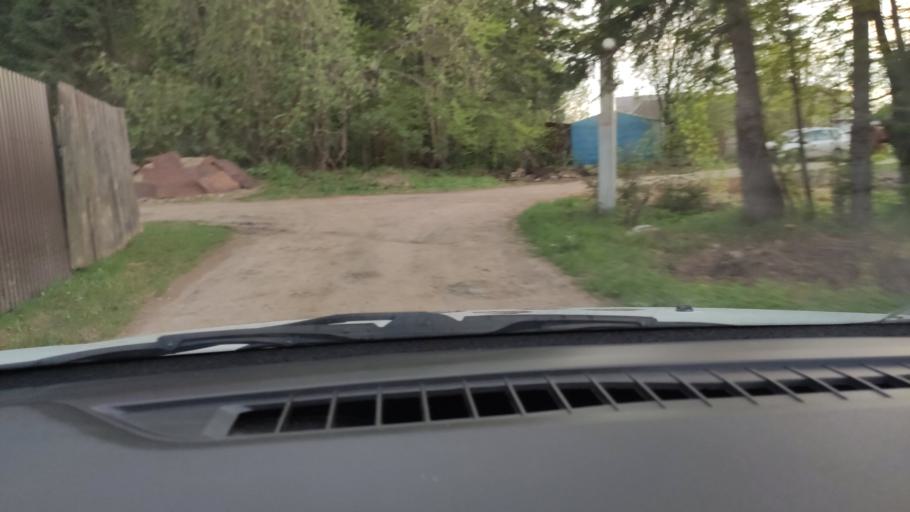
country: RU
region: Perm
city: Froly
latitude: 57.9521
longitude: 56.2902
